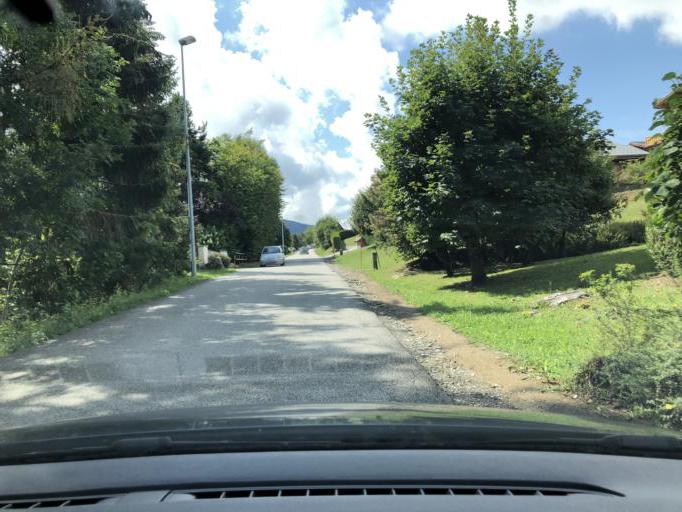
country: FR
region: Rhone-Alpes
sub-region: Departement de la Haute-Savoie
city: Combloux
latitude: 45.8883
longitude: 6.6364
